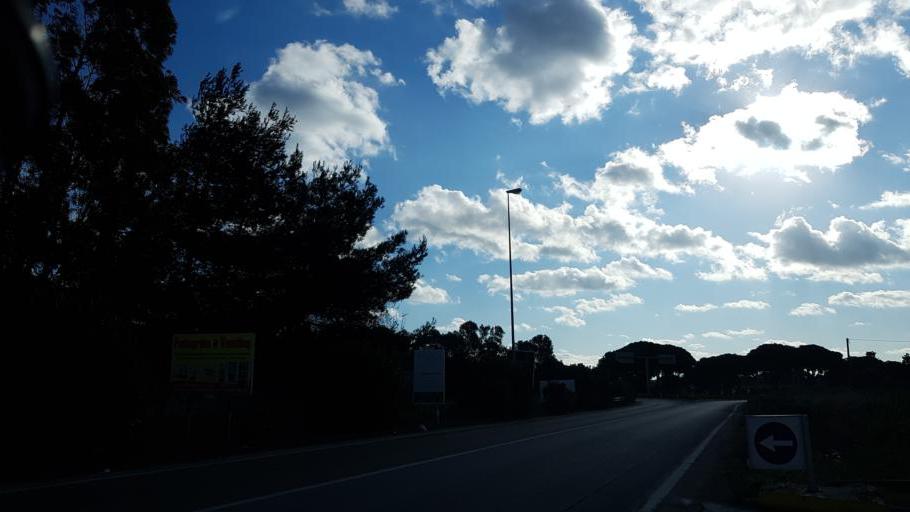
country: IT
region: Apulia
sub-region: Provincia di Brindisi
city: Brindisi
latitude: 40.6585
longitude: 17.9275
